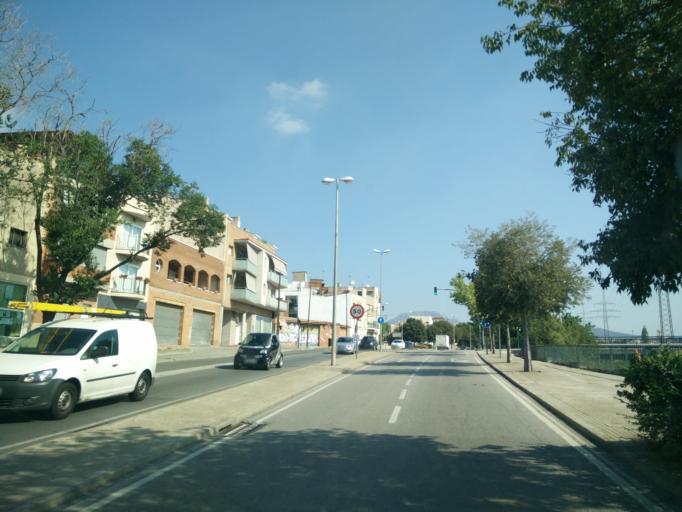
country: ES
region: Catalonia
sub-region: Provincia de Barcelona
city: Terrassa
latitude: 41.5597
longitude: 2.0329
